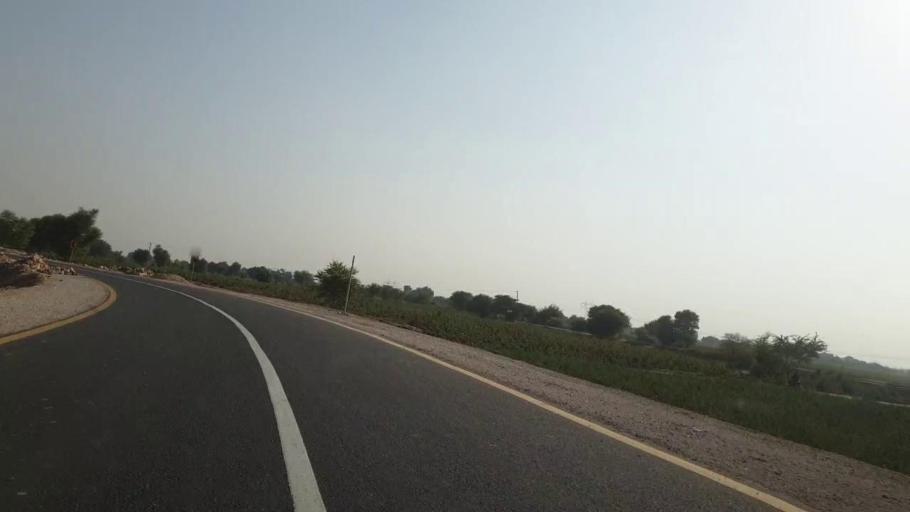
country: PK
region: Sindh
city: Bhan
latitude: 26.4836
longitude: 67.7794
